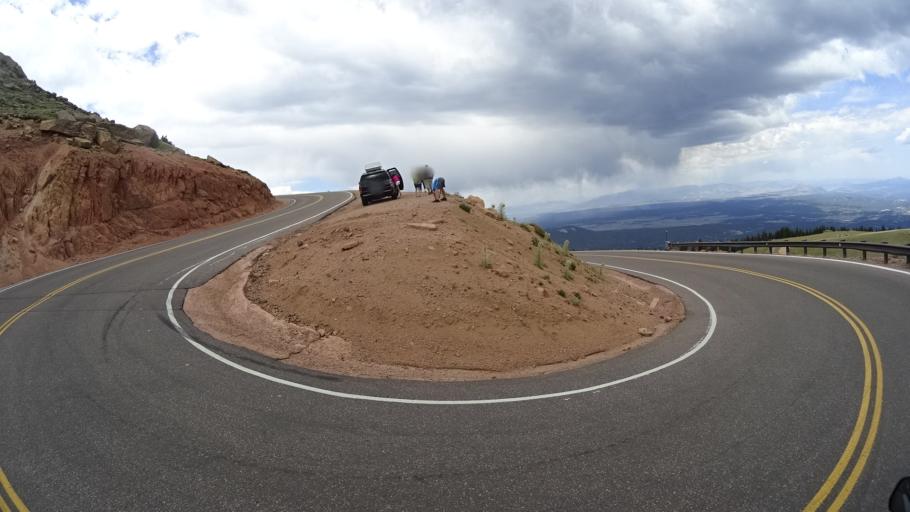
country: US
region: Colorado
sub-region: El Paso County
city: Cascade-Chipita Park
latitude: 38.8752
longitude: -105.0654
